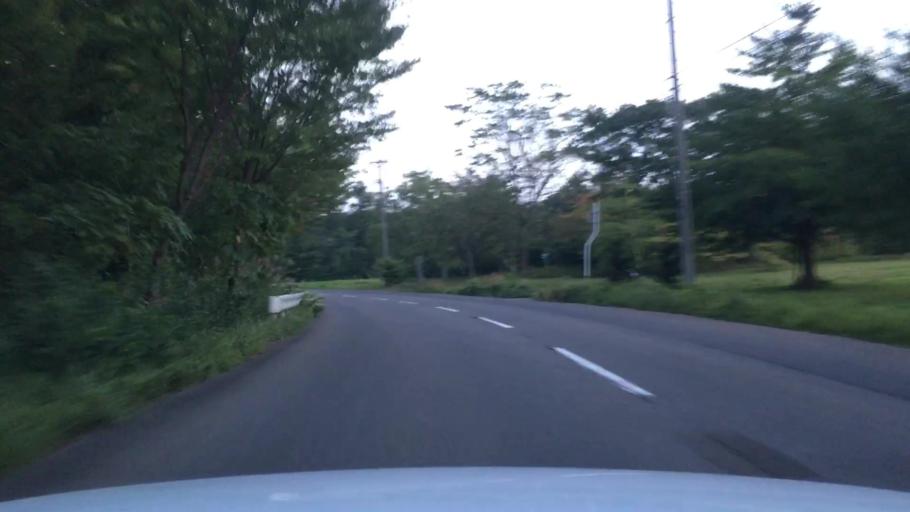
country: JP
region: Aomori
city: Shimokizukuri
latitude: 40.6881
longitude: 140.3630
